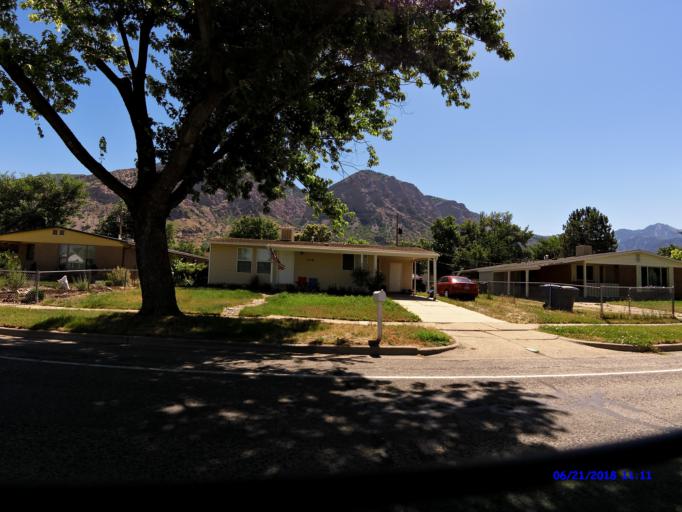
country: US
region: Utah
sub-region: Weber County
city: Harrisville
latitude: 41.2699
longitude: -111.9591
